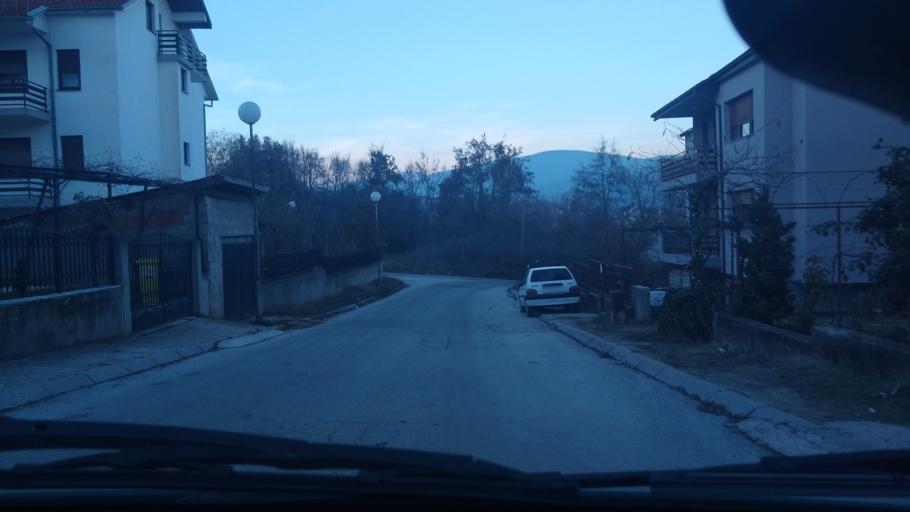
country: MK
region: Bitola
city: Bitola
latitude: 41.0254
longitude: 21.3039
